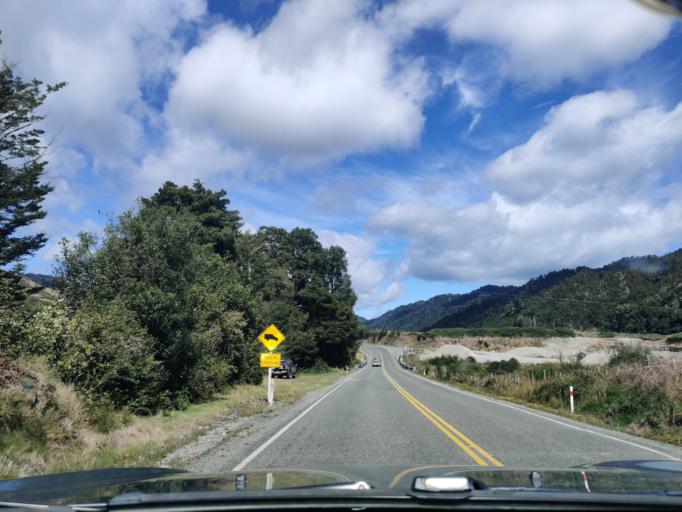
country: NZ
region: Tasman
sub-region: Tasman District
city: Wakefield
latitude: -41.7468
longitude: 172.3958
